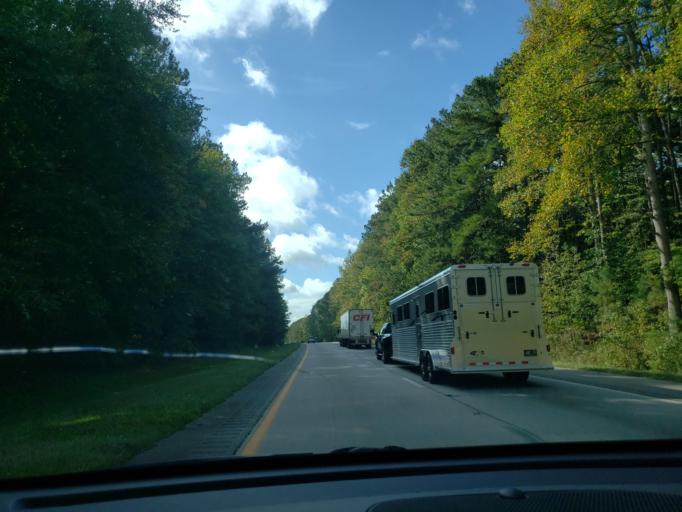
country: US
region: North Carolina
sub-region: Granville County
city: Oxford
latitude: 36.3224
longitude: -78.5140
